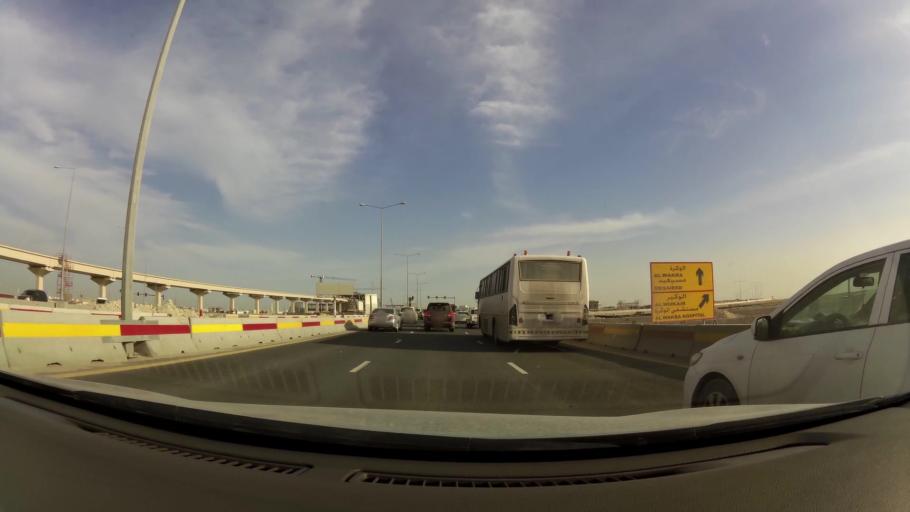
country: QA
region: Al Wakrah
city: Al Wakrah
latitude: 25.1978
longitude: 51.5926
